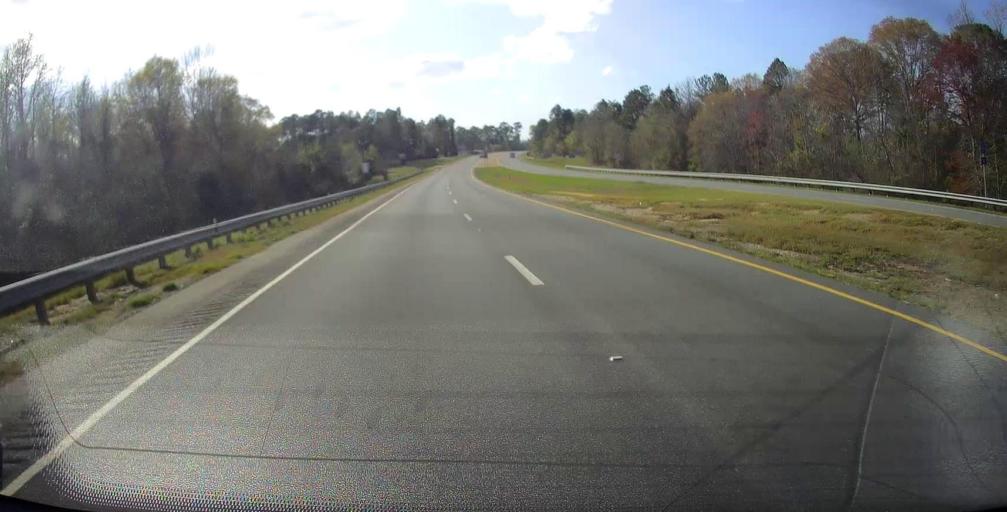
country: US
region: Georgia
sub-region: Telfair County
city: Helena
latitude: 32.1018
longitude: -83.0519
